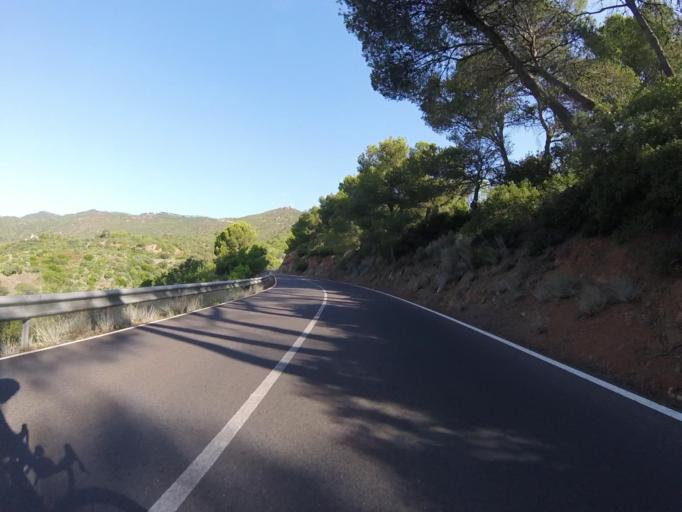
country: ES
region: Valencia
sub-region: Provincia de Castello
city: Benicassim
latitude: 40.0780
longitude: 0.0435
